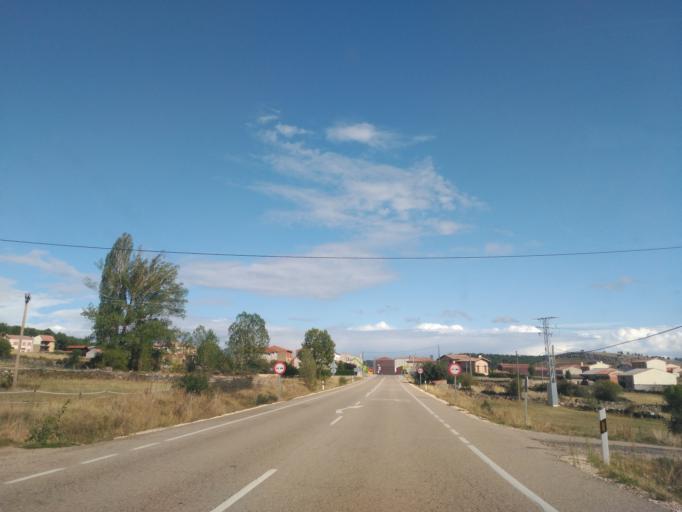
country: ES
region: Castille and Leon
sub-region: Provincia de Burgos
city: Hontoria del Pinar
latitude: 41.8500
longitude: -3.1692
